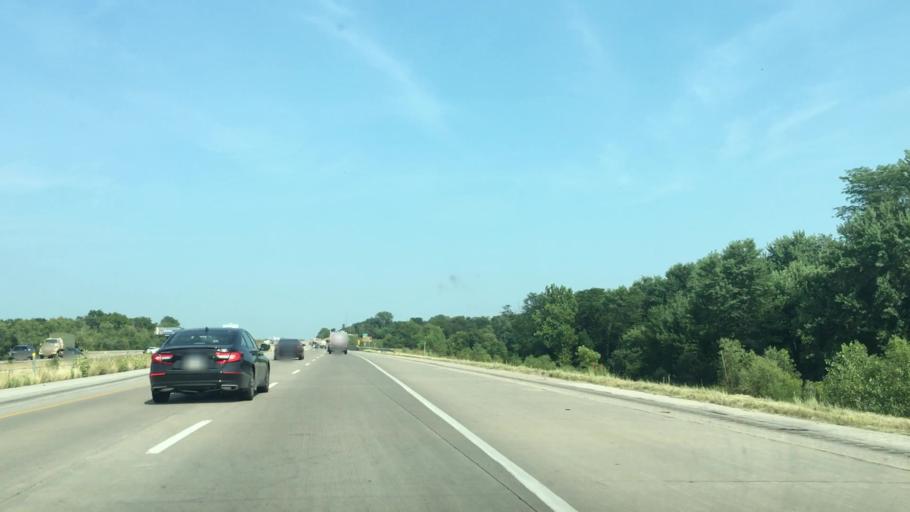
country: US
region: Iowa
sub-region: Cedar County
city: Tipton
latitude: 41.6445
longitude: -91.1365
